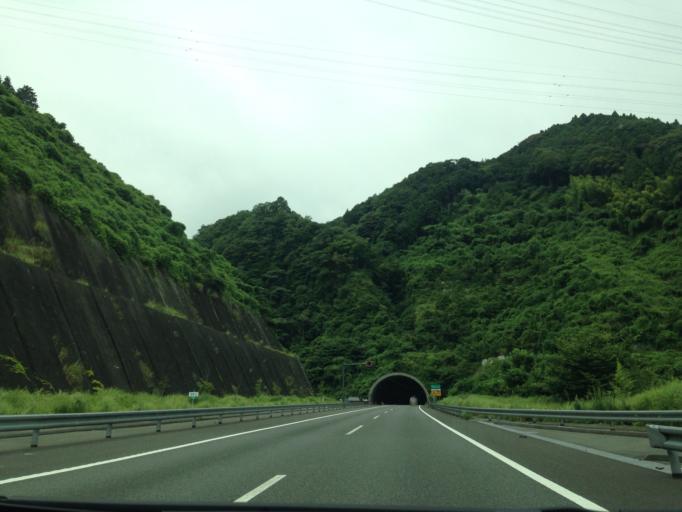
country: JP
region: Shizuoka
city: Fujinomiya
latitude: 35.1665
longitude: 138.5919
